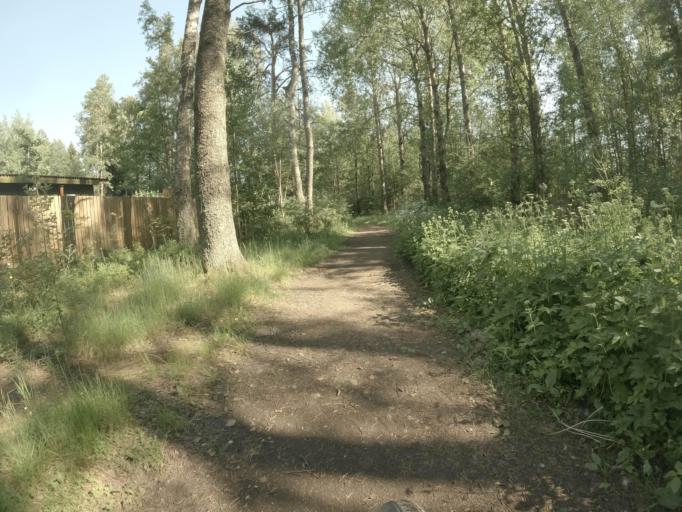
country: RU
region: Leningrad
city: Yakovlevo
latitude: 60.4651
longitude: 29.2793
